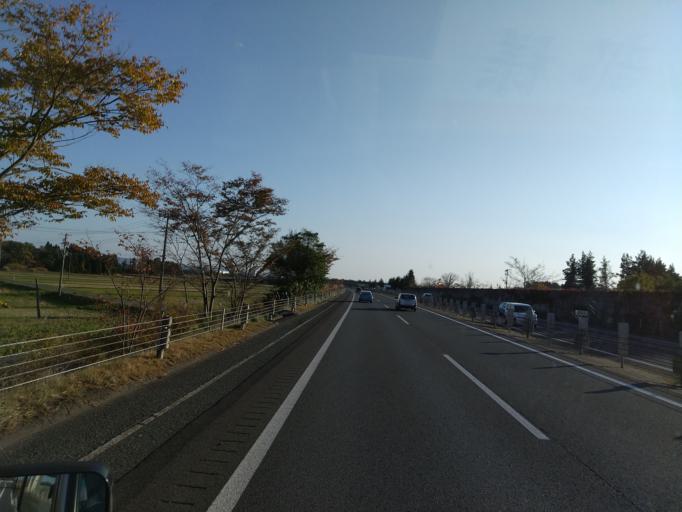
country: JP
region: Iwate
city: Hanamaki
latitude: 39.4650
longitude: 141.1085
